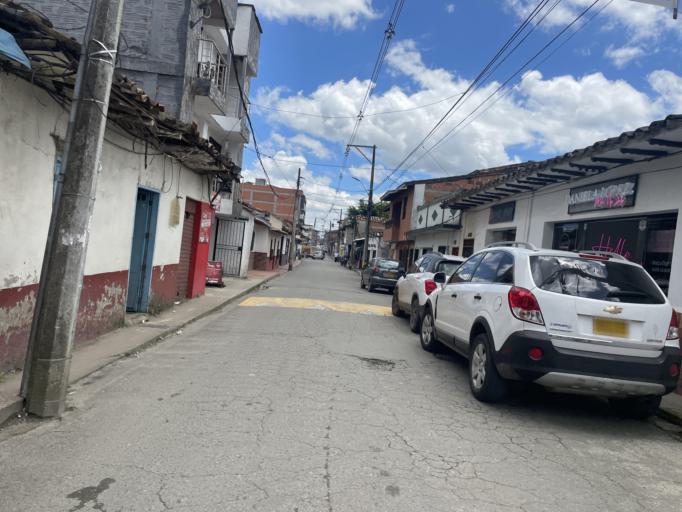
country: CO
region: Antioquia
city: La Ceja
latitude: 6.0254
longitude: -75.4328
